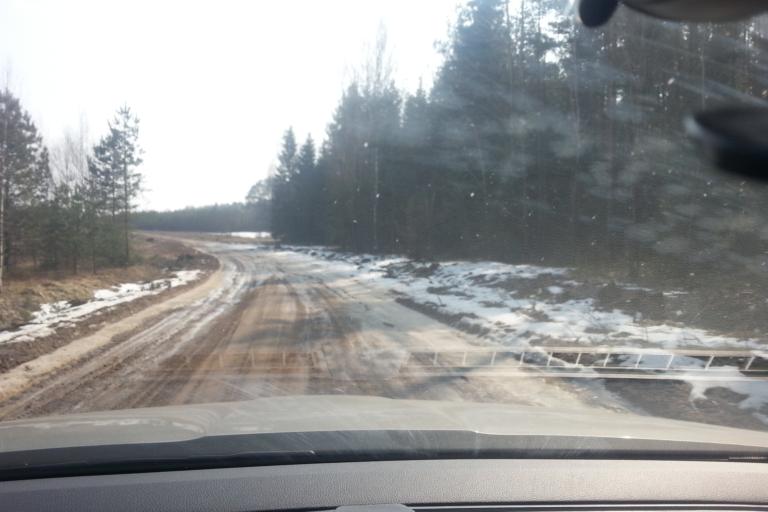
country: LT
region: Vilnius County
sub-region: Trakai
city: Rudiskes
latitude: 54.5022
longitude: 24.9593
